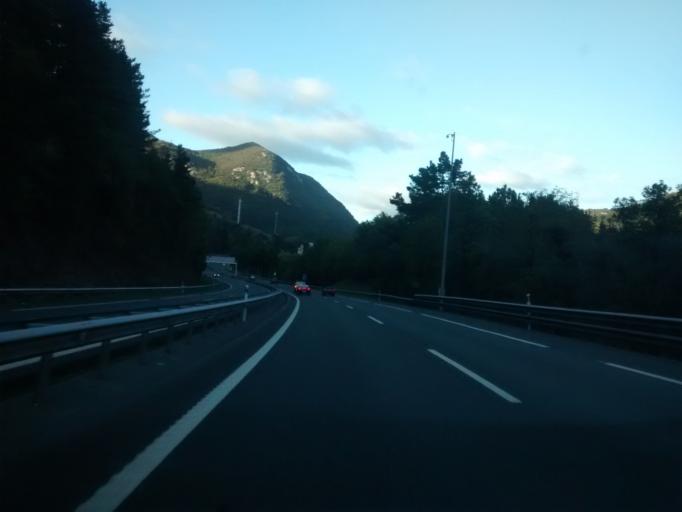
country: ES
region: Basque Country
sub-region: Provincia de Guipuzcoa
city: Mendaro
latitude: 43.2456
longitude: -2.3952
